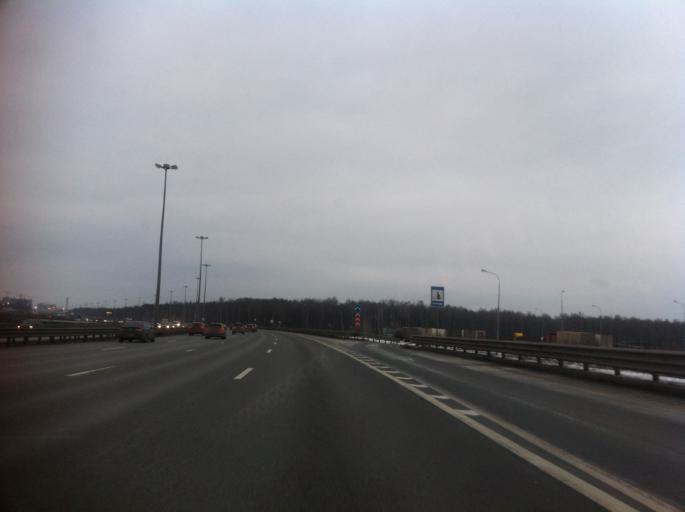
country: RU
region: Leningrad
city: Rybatskoye
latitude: 59.8668
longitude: 30.5302
